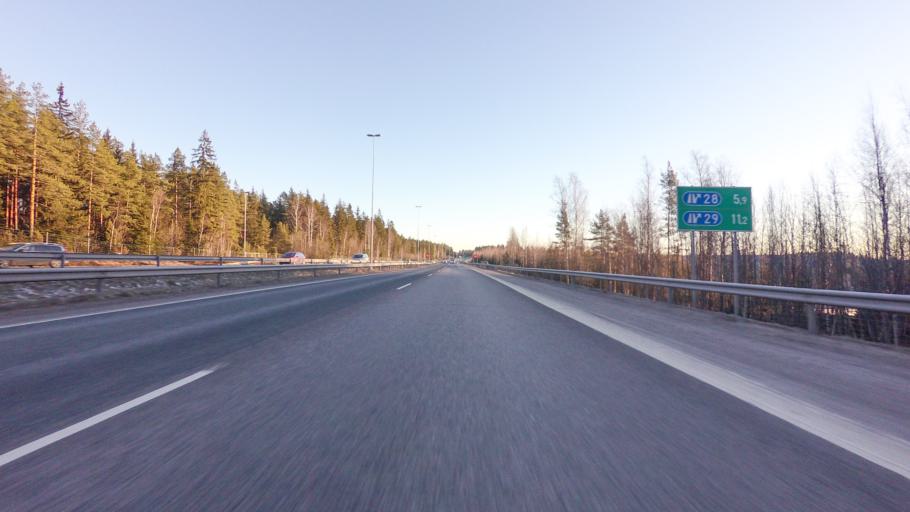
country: FI
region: Uusimaa
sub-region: Helsinki
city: Kirkkonummi
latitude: 60.2715
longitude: 24.4600
